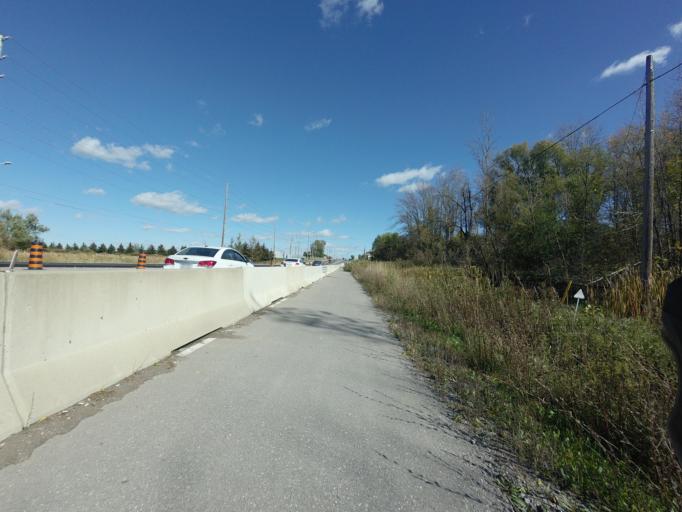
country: CA
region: Ontario
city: Ajax
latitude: 43.8571
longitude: -78.9586
